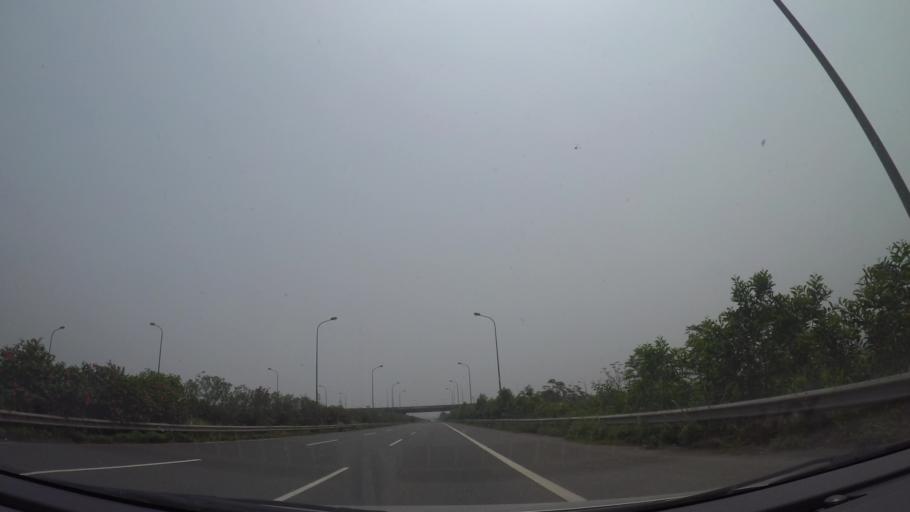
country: VN
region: Ha Noi
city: Quoc Oai
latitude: 21.0016
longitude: 105.6228
